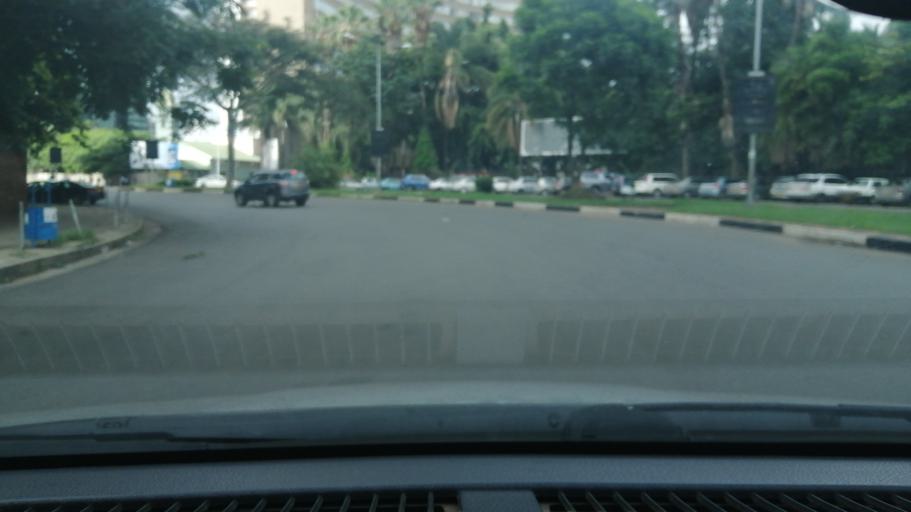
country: ZW
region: Harare
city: Harare
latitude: -17.8256
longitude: 31.0484
